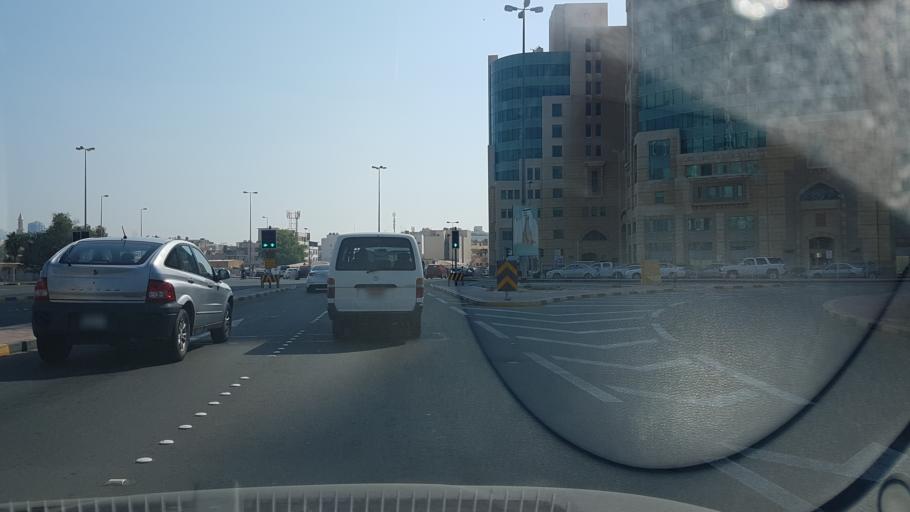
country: BH
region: Manama
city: Manama
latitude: 26.2379
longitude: 50.5809
